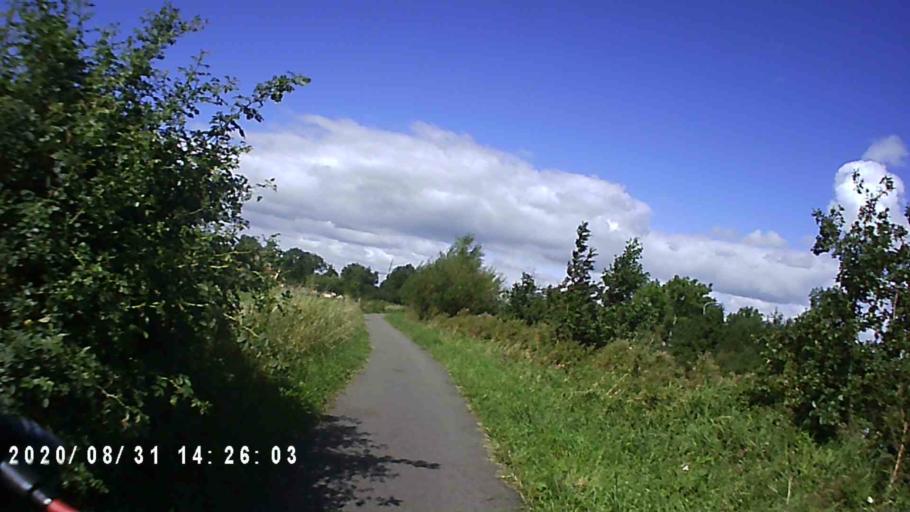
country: NL
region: Groningen
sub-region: Gemeente Zuidhorn
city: Zuidhorn
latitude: 53.2133
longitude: 6.4103
